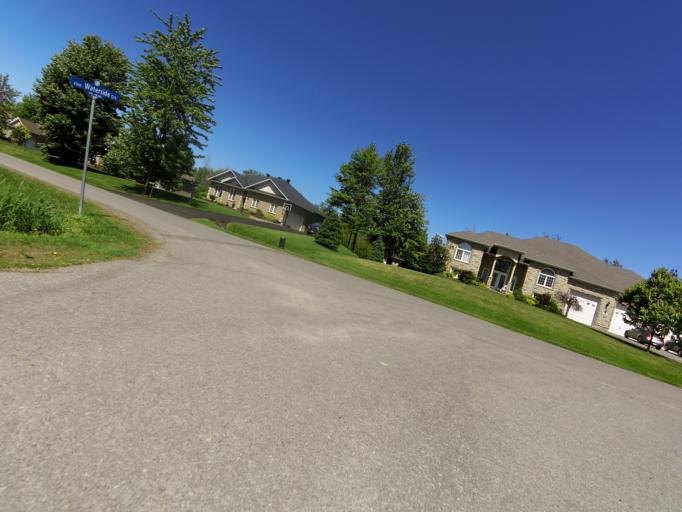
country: CA
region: Ontario
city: Ottawa
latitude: 45.2689
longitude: -75.5886
